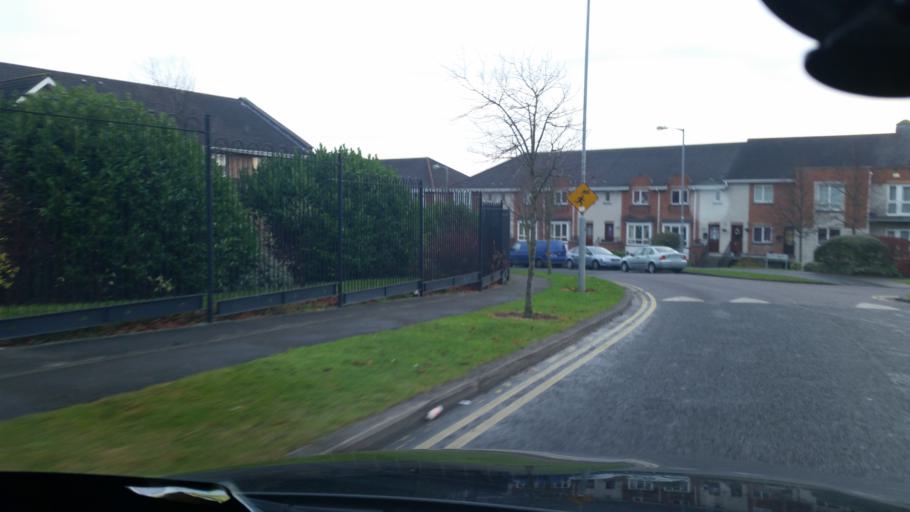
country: IE
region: Leinster
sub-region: Dublin City
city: Finglas
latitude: 53.4060
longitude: -6.2995
